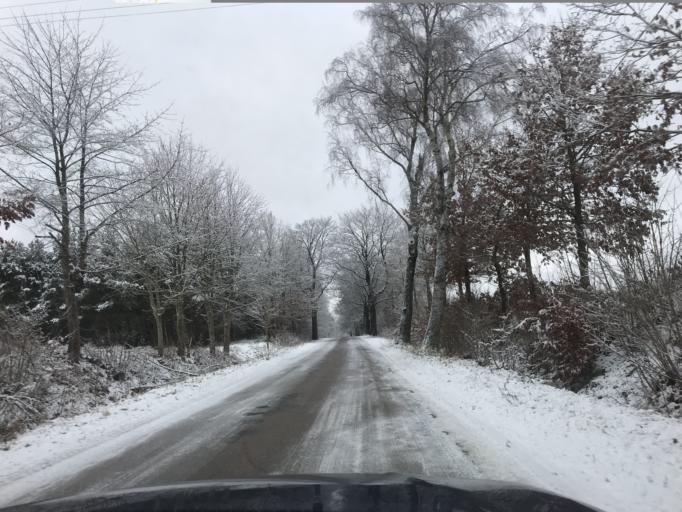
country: PL
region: Pomeranian Voivodeship
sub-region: Powiat bytowski
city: Parchowo
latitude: 54.2355
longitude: 17.5751
